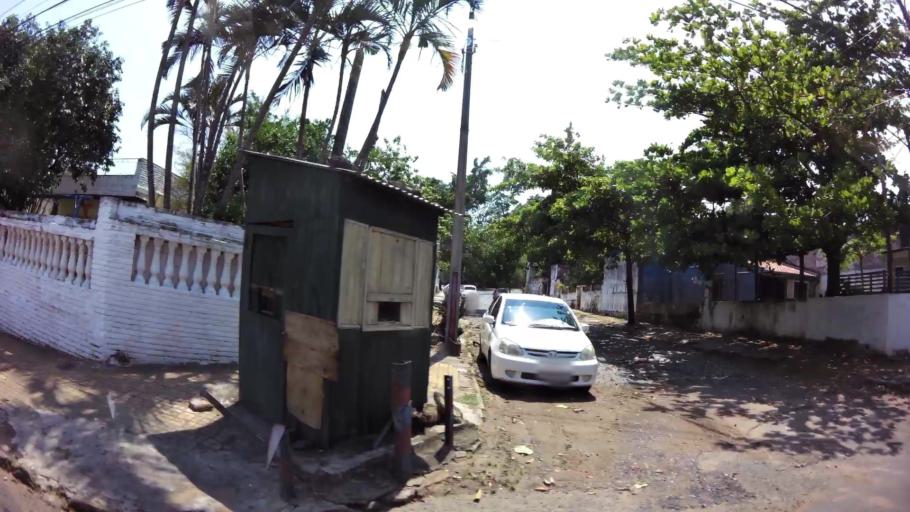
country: PY
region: Asuncion
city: Asuncion
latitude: -25.3018
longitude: -57.6377
